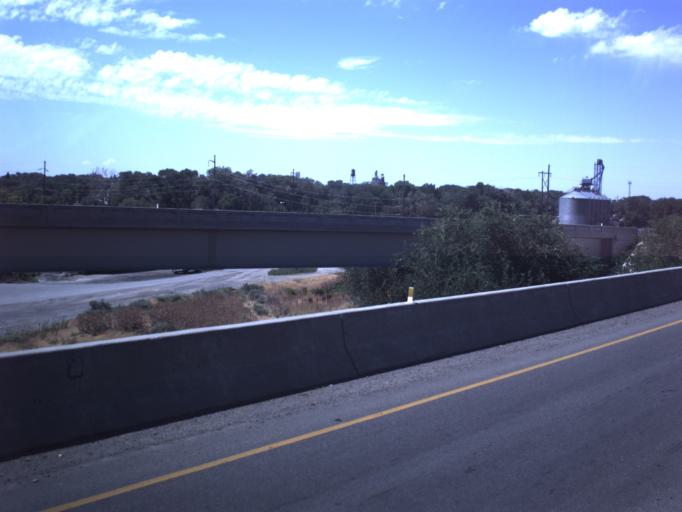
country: US
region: Utah
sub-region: Weber County
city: Ogden
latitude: 41.2318
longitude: -111.9877
